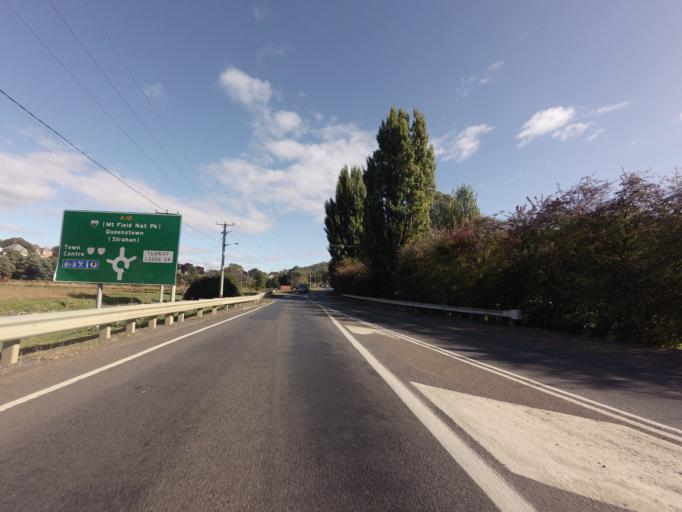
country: AU
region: Tasmania
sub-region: Derwent Valley
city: New Norfolk
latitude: -42.7790
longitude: 147.0717
